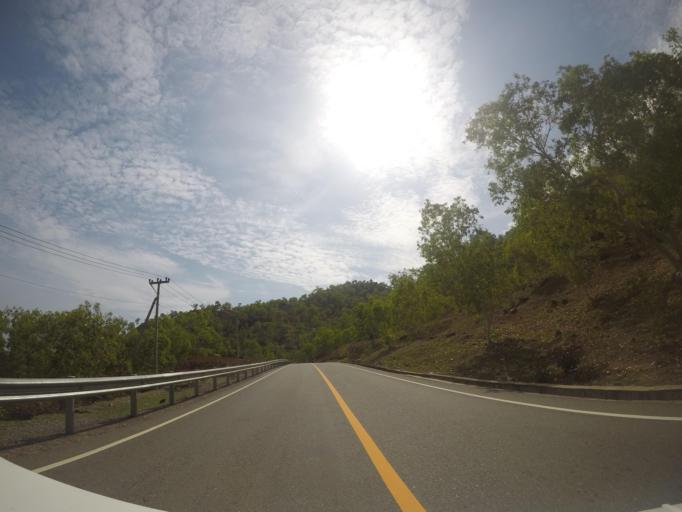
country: TL
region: Manatuto
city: Manatuto
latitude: -8.4780
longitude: 125.8981
